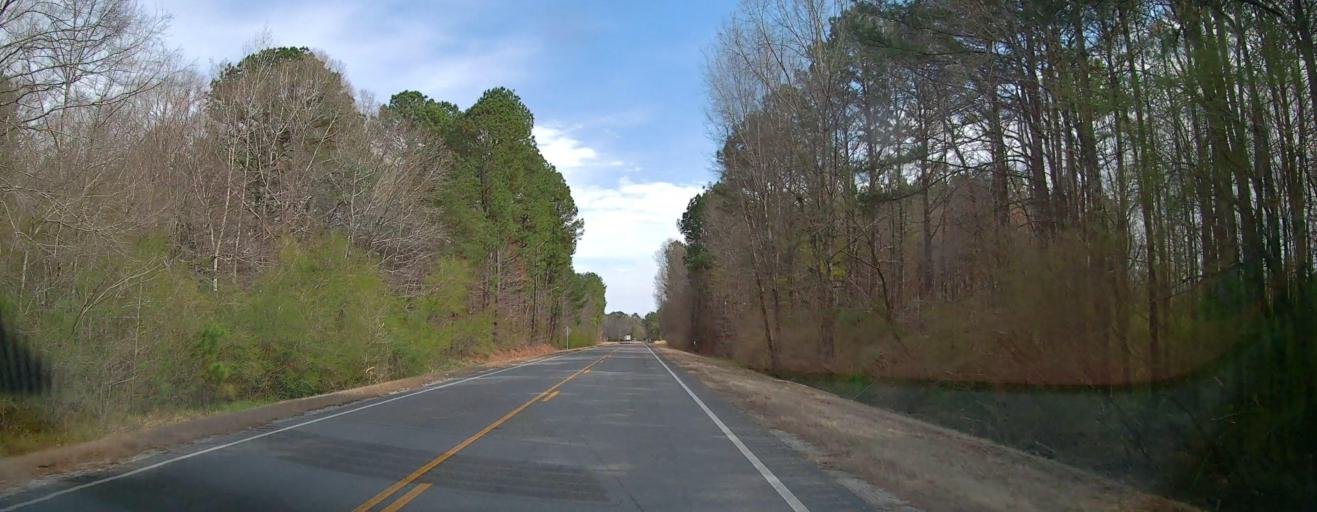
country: US
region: Alabama
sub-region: Walker County
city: Carbon Hill
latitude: 33.9047
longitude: -87.5509
